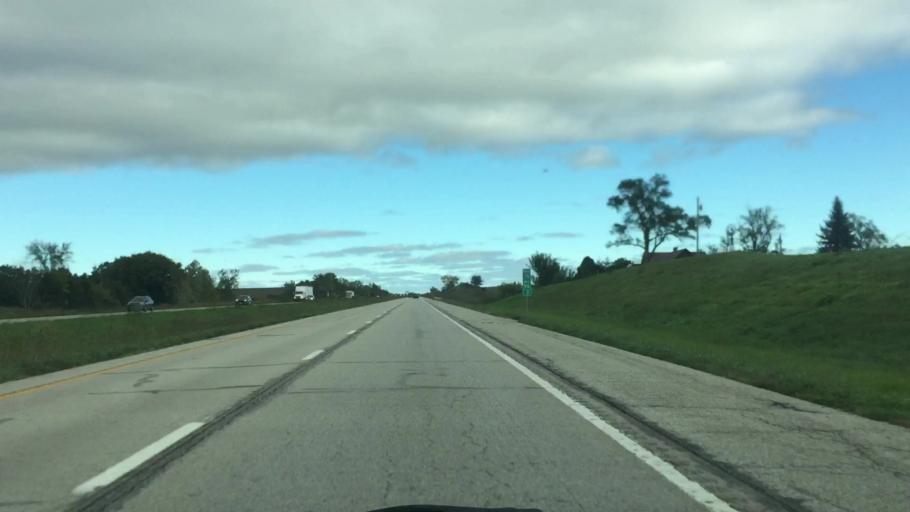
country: US
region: Missouri
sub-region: Harrison County
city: Bethany
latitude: 40.3227
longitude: -94.0114
